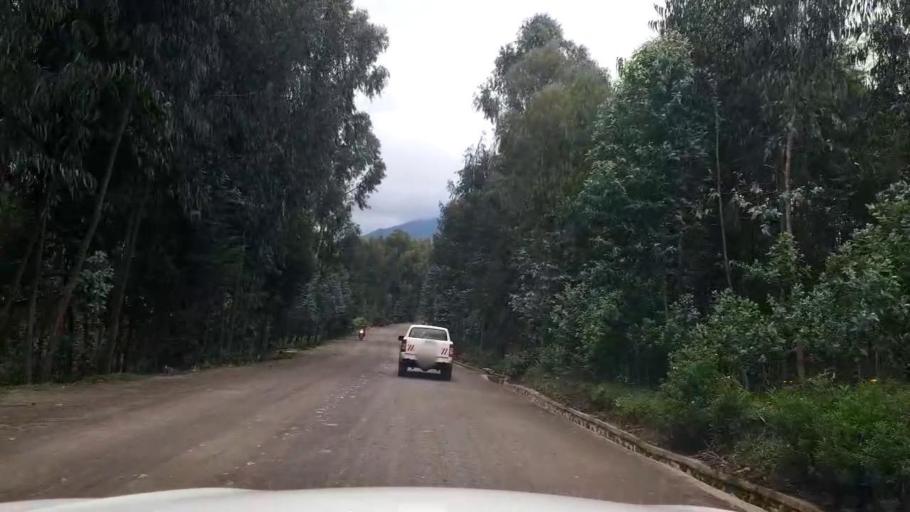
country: RW
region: Northern Province
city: Musanze
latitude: -1.4433
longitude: 29.5361
